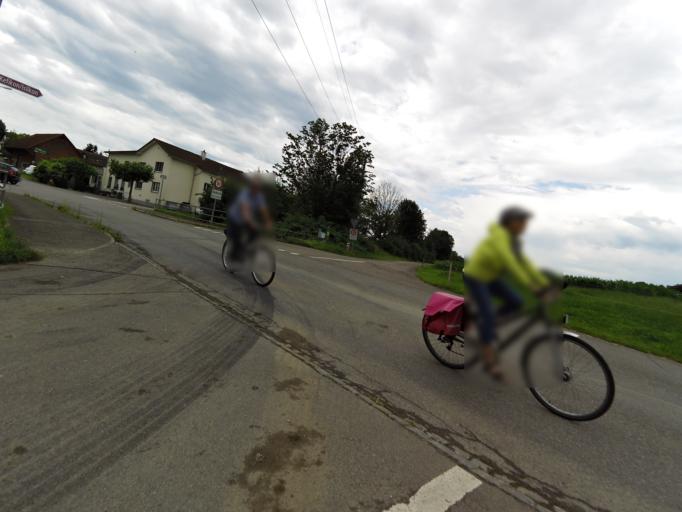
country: CH
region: Thurgau
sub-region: Frauenfeld District
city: Gachnang
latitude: 47.5543
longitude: 8.8608
